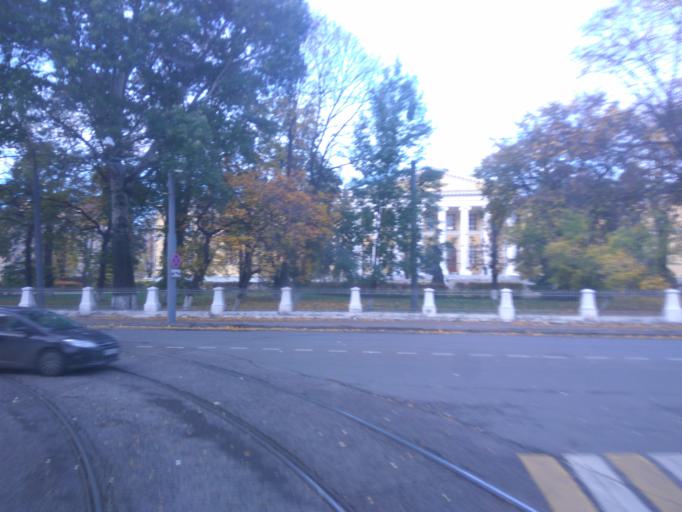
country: RU
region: Moscow
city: Mar'ina Roshcha
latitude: 55.7829
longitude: 37.6110
